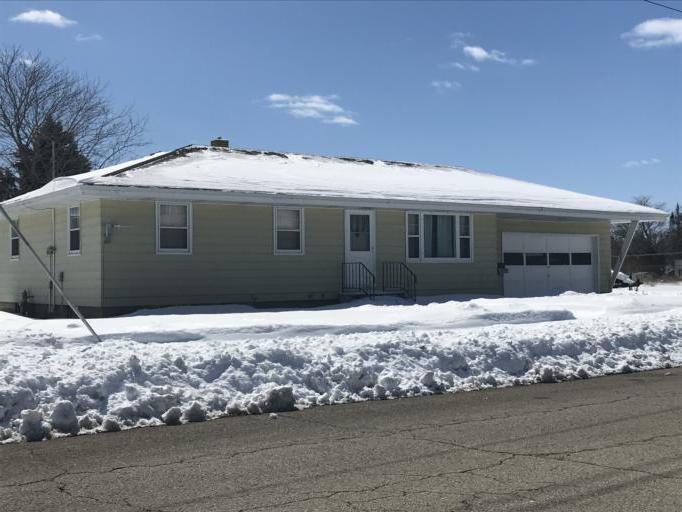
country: US
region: Wisconsin
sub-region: Oconto County
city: Oconto
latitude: 44.8901
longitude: -87.8809
